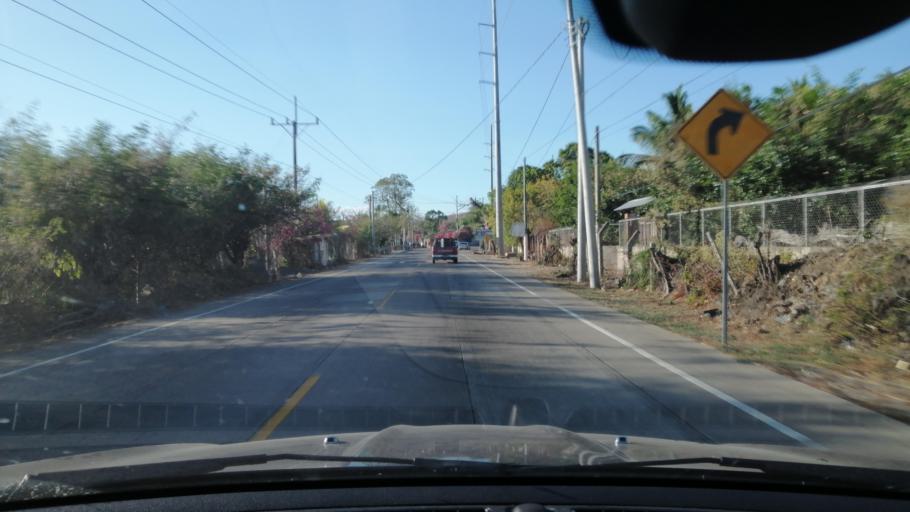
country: SV
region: Santa Ana
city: Metapan
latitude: 14.2400
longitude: -89.4720
